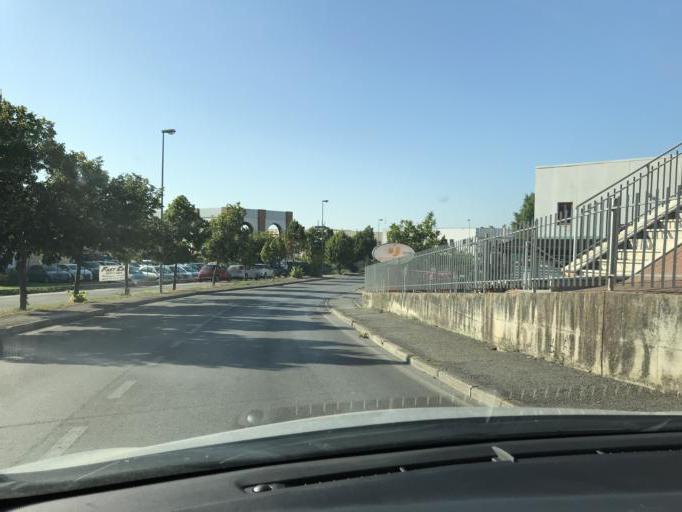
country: IT
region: Umbria
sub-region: Provincia di Perugia
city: Chiugiana-La Commenda
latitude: 43.1018
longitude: 12.3172
